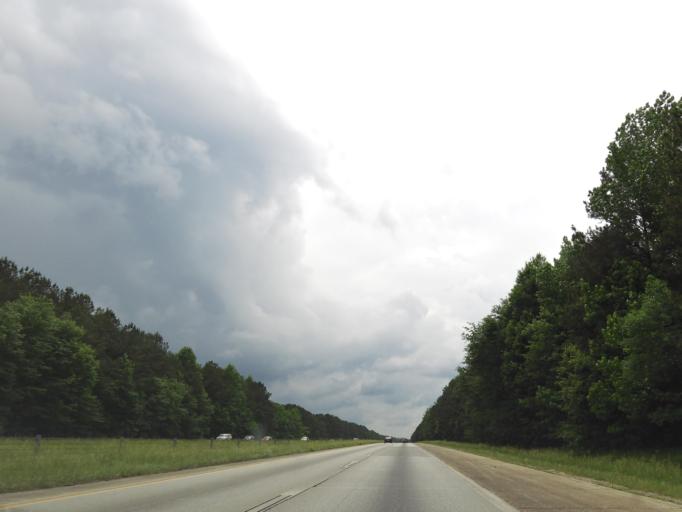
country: US
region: Georgia
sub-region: Haralson County
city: Bremen
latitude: 33.6897
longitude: -85.1061
